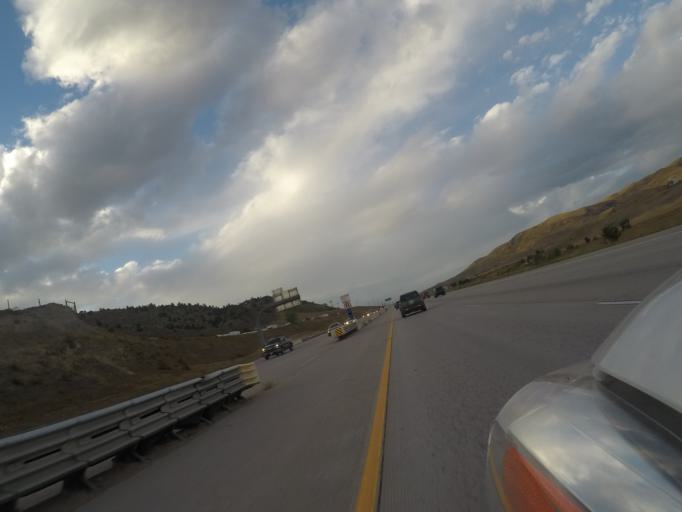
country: US
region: Colorado
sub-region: Jefferson County
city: West Pleasant View
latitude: 39.6698
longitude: -105.1874
